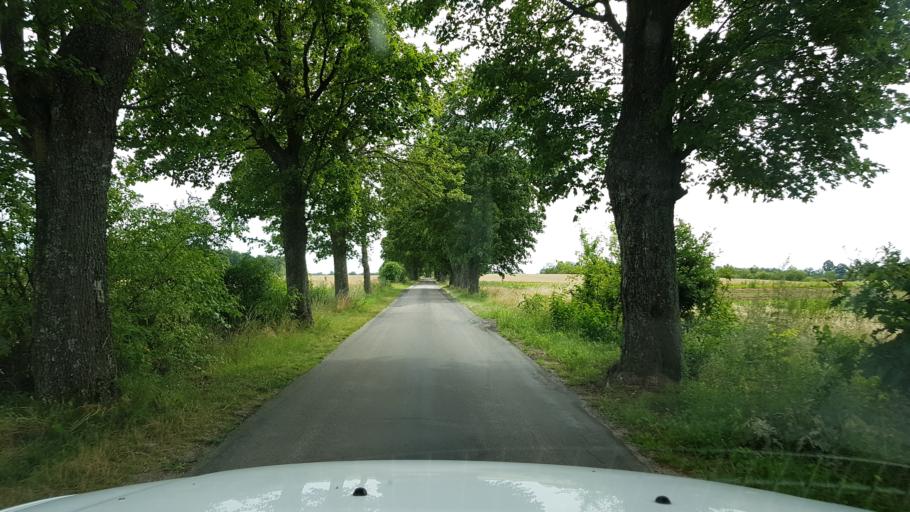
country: PL
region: West Pomeranian Voivodeship
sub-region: Powiat koszalinski
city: Mielno
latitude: 54.1652
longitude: 16.0609
